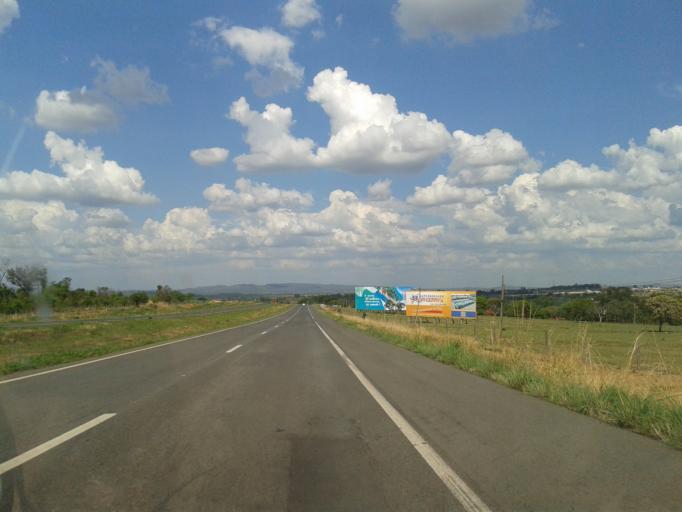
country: BR
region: Goias
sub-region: Caldas Novas
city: Caldas Novas
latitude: -17.7151
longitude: -48.6738
